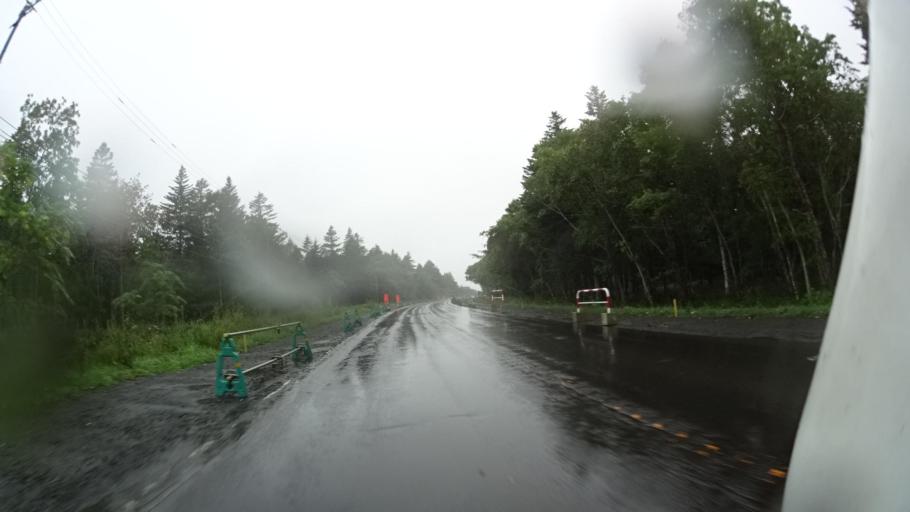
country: JP
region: Hokkaido
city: Nemuro
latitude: 43.2533
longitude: 145.3767
